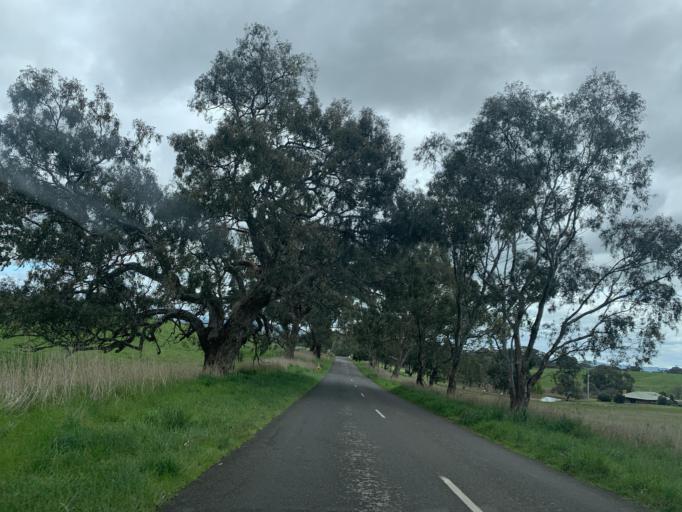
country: AU
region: Victoria
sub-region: Whittlesea
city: Whittlesea
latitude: -37.1859
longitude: 145.0219
